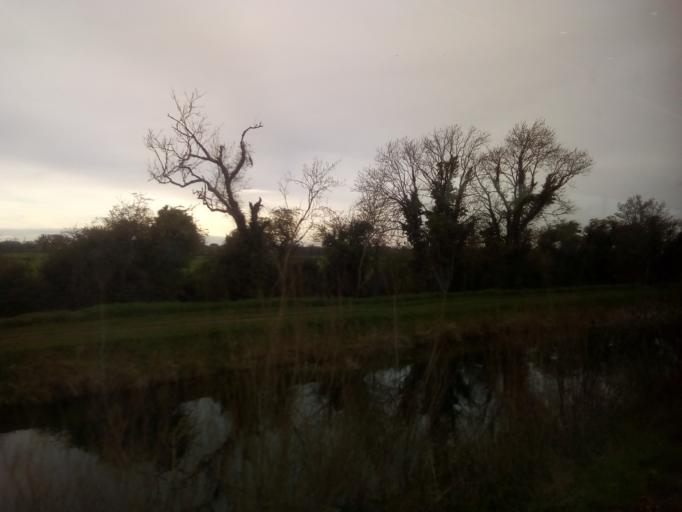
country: IE
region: Leinster
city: Lucan
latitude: 53.3785
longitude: -6.4475
